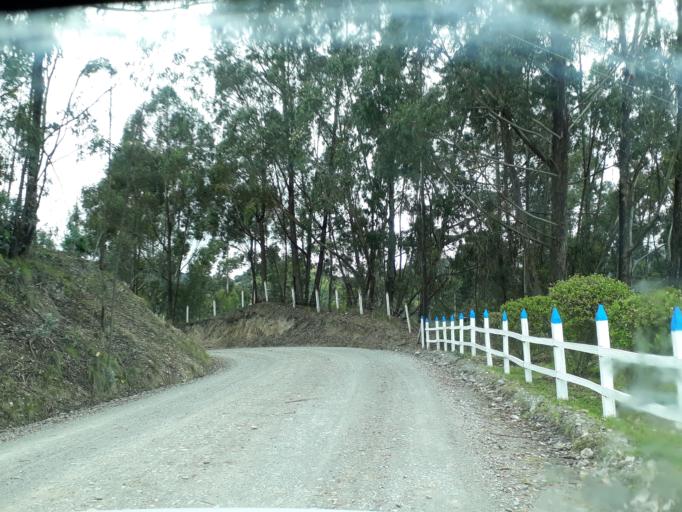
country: CO
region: Cundinamarca
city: La Mesa
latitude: 5.2916
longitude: -73.9060
